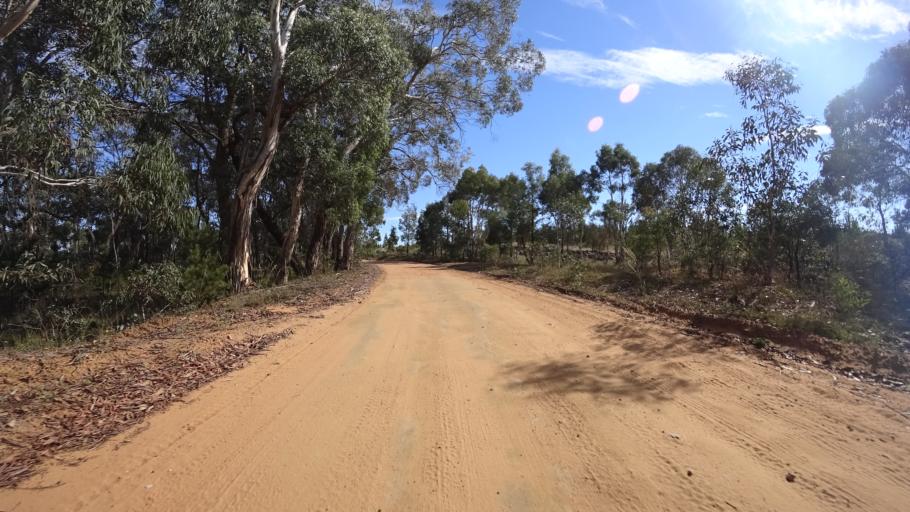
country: AU
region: New South Wales
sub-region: Lithgow
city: Lithgow
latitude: -33.3562
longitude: 150.2532
